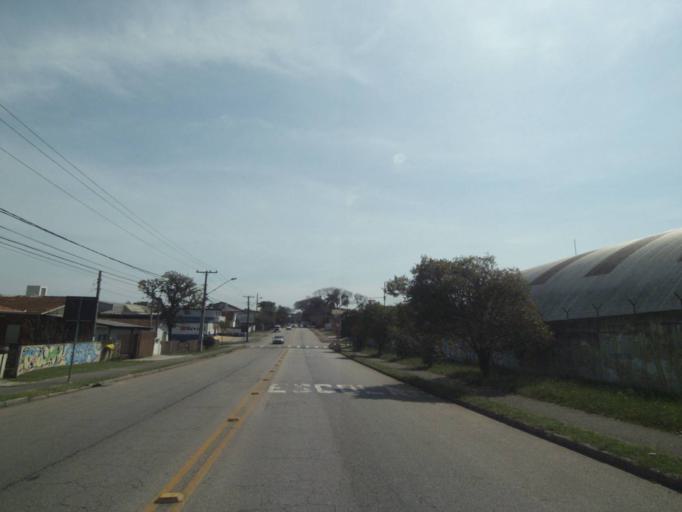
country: BR
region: Parana
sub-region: Curitiba
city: Curitiba
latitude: -25.4639
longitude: -49.3081
